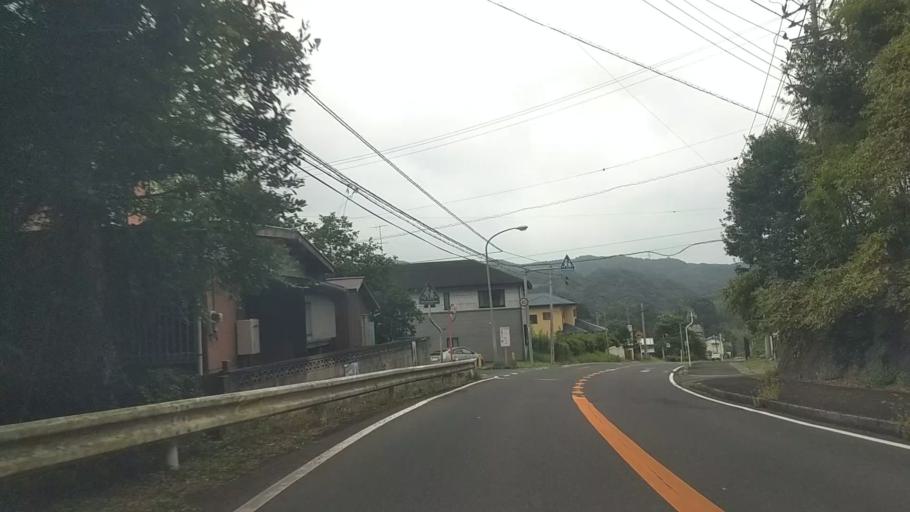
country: JP
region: Chiba
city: Kisarazu
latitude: 35.2828
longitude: 140.0802
